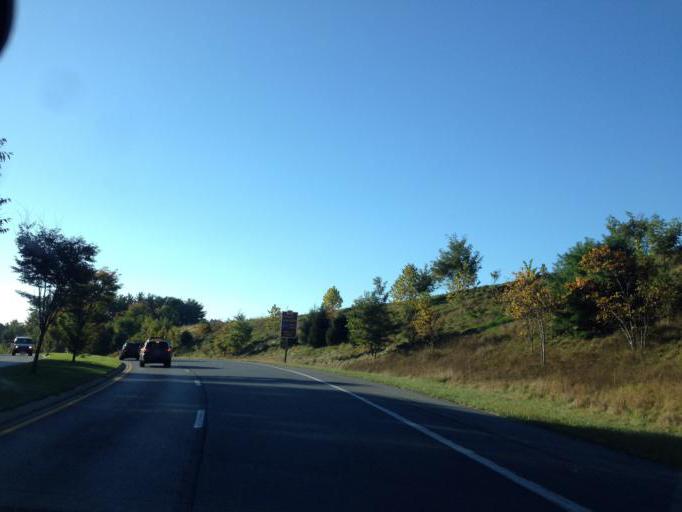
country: US
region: Maryland
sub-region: Carroll County
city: Sykesville
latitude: 39.3785
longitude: -76.9684
